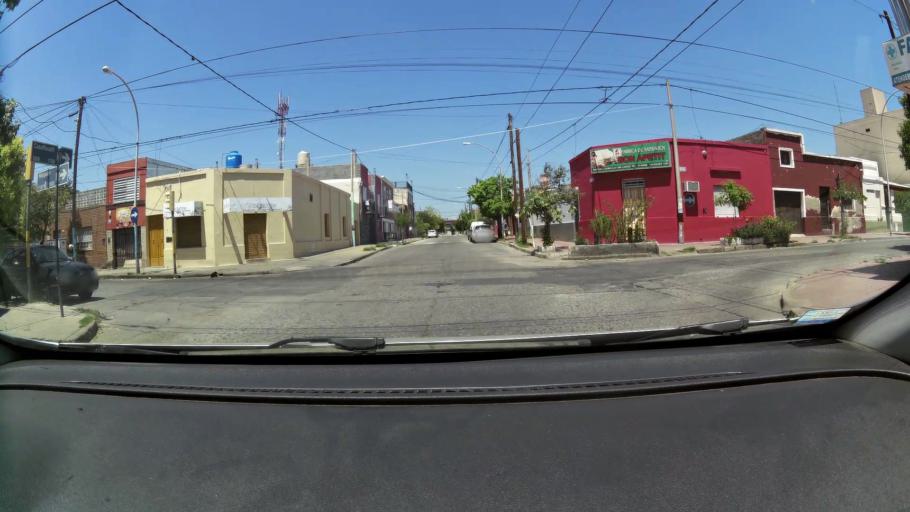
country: AR
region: Cordoba
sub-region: Departamento de Capital
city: Cordoba
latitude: -31.3992
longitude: -64.2005
